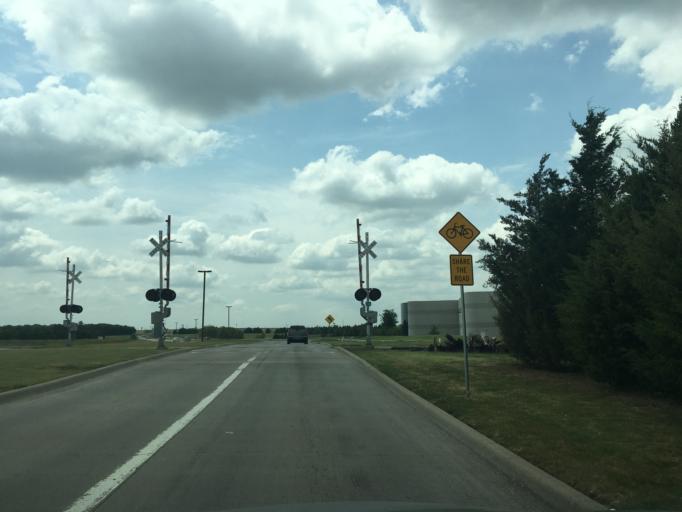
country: US
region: Texas
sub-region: Rockwall County
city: Rockwall
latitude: 32.9241
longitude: -96.4361
